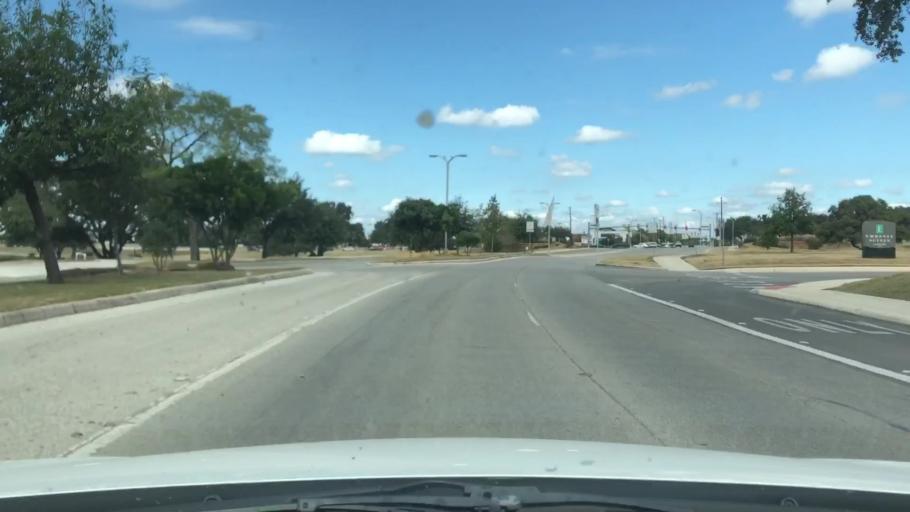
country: US
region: Texas
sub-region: Bexar County
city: San Antonio
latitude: 29.3494
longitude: -98.4482
